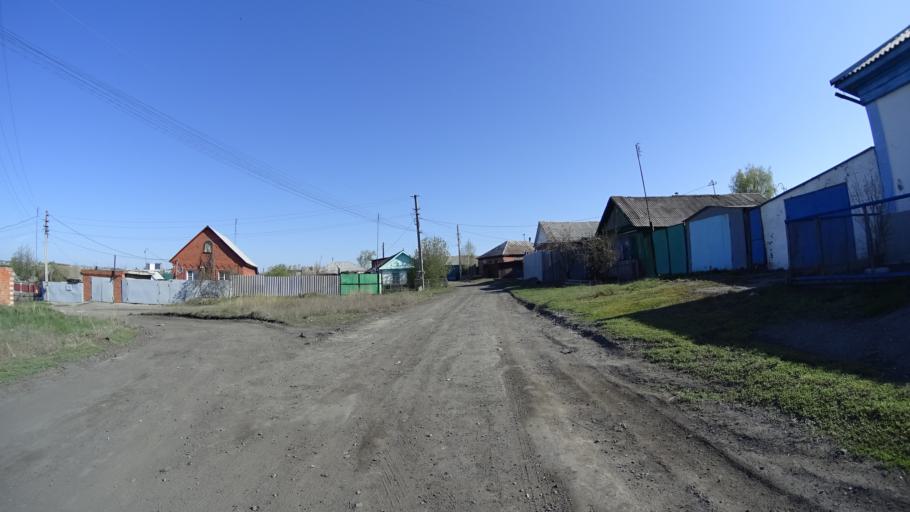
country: RU
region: Chelyabinsk
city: Troitsk
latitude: 54.0856
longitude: 61.5971
